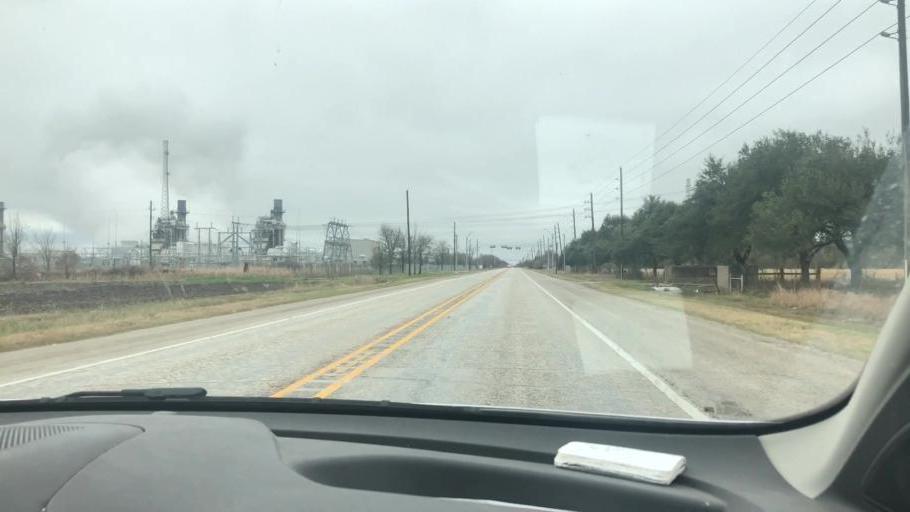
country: US
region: Texas
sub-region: Wharton County
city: Wharton
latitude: 29.2910
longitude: -96.0726
